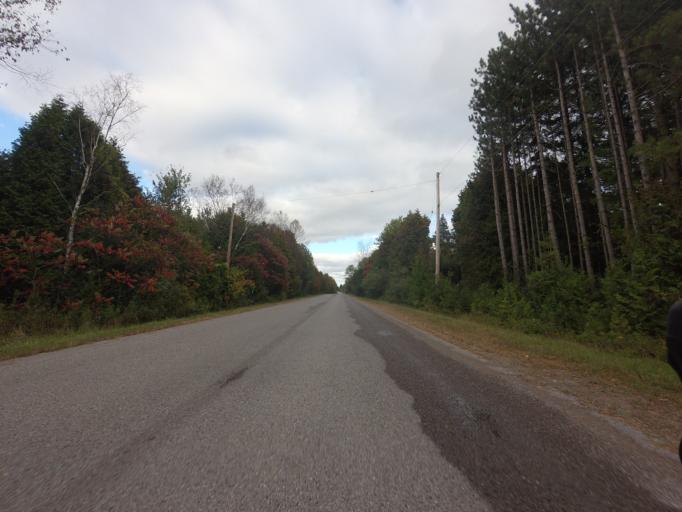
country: CA
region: Ontario
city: Cobourg
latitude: 43.9703
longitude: -78.0427
